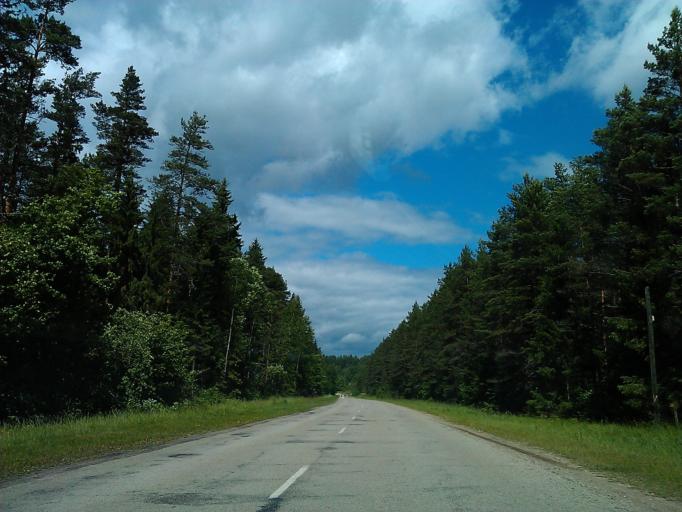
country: LV
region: Talsu Rajons
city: Sabile
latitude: 57.0786
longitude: 22.5297
